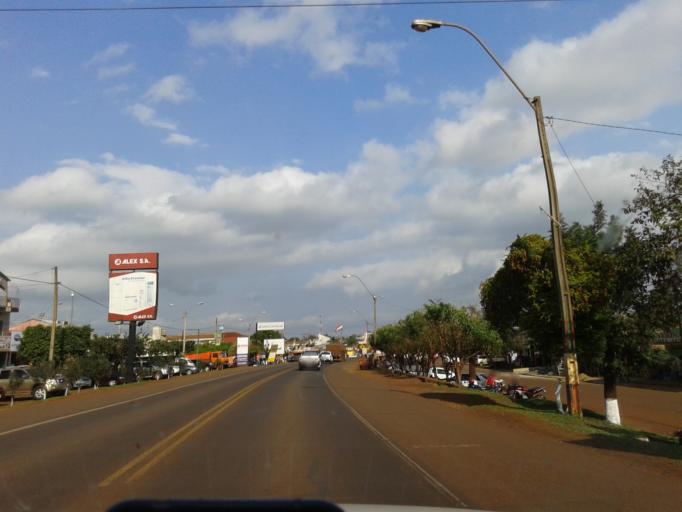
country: PY
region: Itapua
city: Arquitecto Tomas Romero Pereira
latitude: -26.5305
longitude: -55.2599
